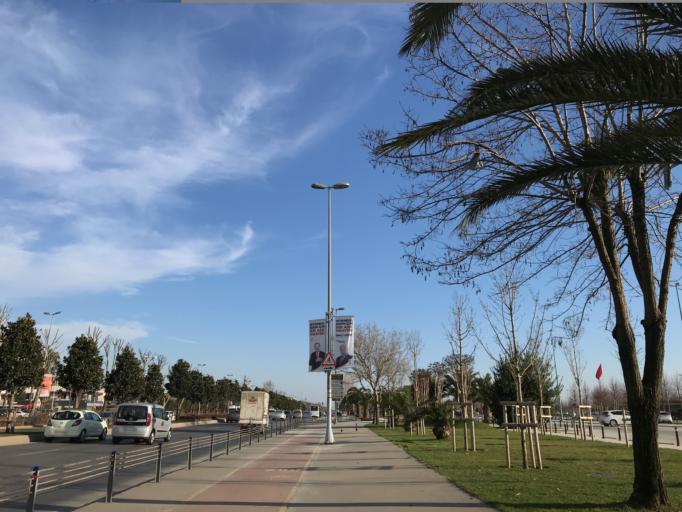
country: TR
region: Istanbul
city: Maltepe
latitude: 40.9285
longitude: 29.1210
